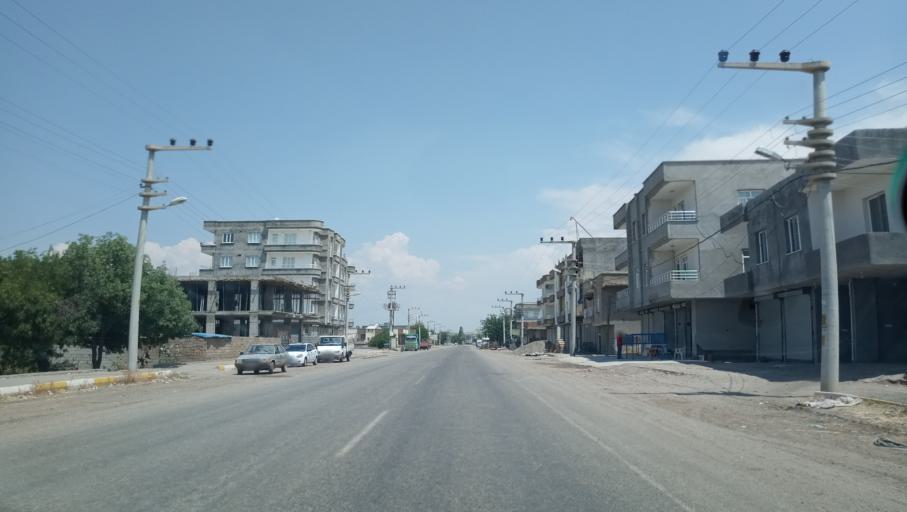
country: TR
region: Diyarbakir
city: Tepe
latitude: 37.7928
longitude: 40.7647
